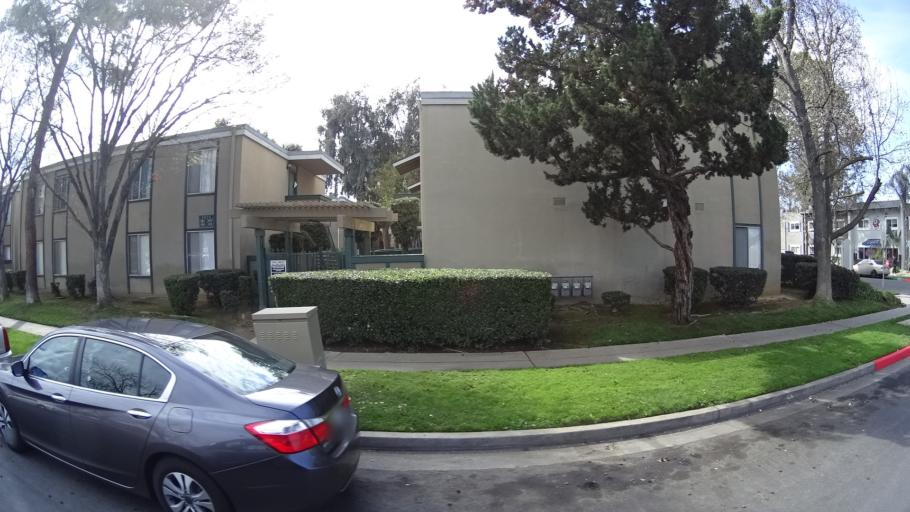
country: US
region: California
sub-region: Fresno County
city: Clovis
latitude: 36.8122
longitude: -119.7585
